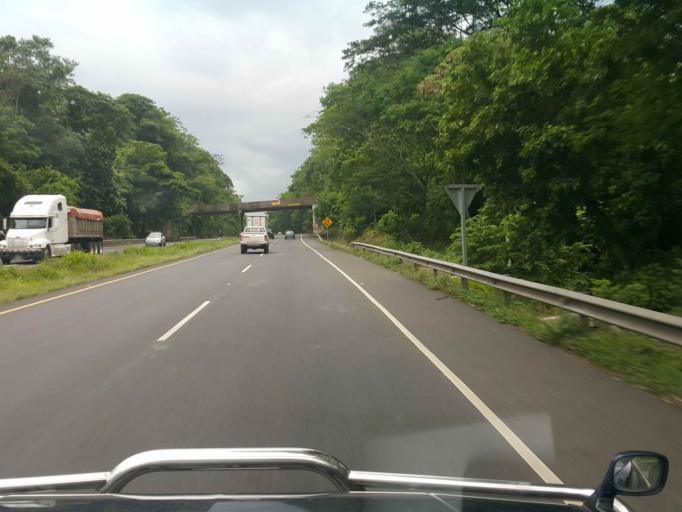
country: CR
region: Alajuela
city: Orotina
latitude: 9.9005
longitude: -84.5435
